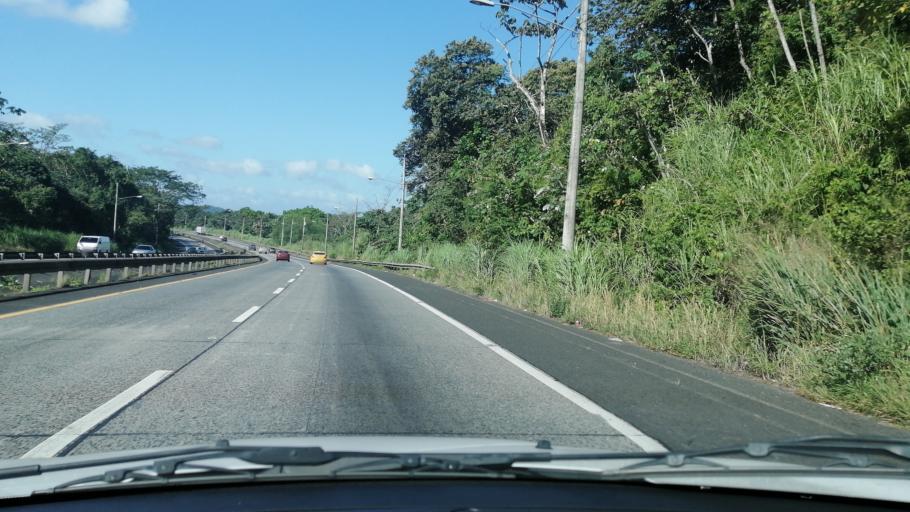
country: PA
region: Panama
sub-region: Distrito de Panama
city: Paraiso
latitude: 9.0414
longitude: -79.5671
